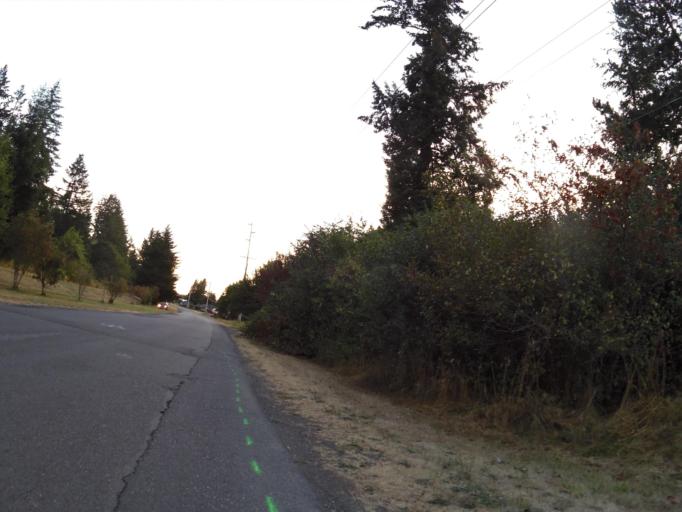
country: US
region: Washington
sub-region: Thurston County
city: Tenino
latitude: 46.8543
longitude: -122.8552
